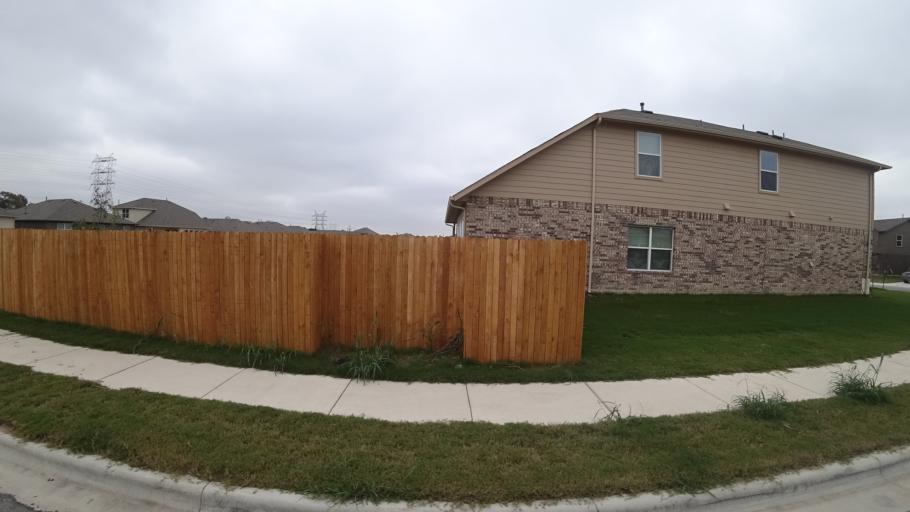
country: US
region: Texas
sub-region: Travis County
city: Pflugerville
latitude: 30.3700
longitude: -97.6486
